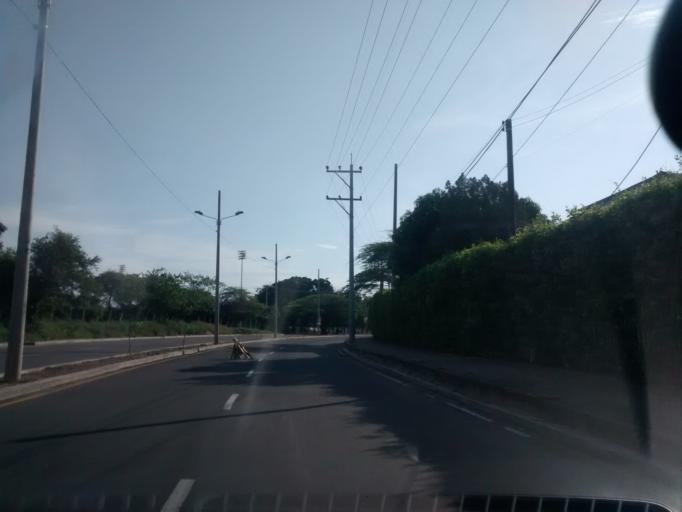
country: CO
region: Cundinamarca
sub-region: Girardot
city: Girardot City
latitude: 4.3074
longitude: -74.8116
